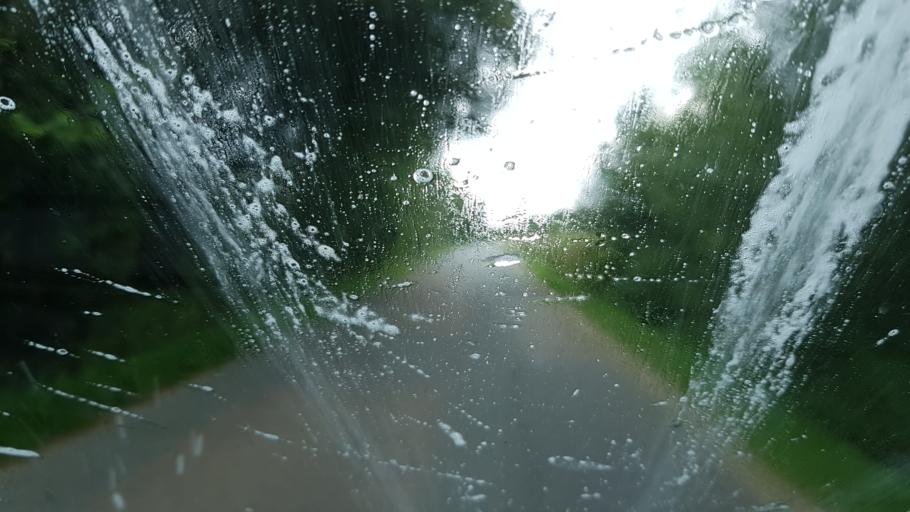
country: DK
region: South Denmark
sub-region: Billund Kommune
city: Grindsted
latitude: 55.6455
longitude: 8.8115
